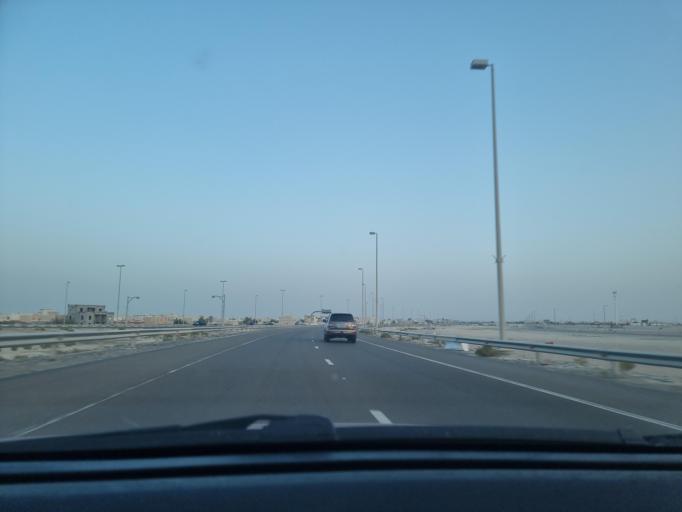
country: AE
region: Abu Dhabi
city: Abu Dhabi
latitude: 24.4106
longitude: 54.7146
